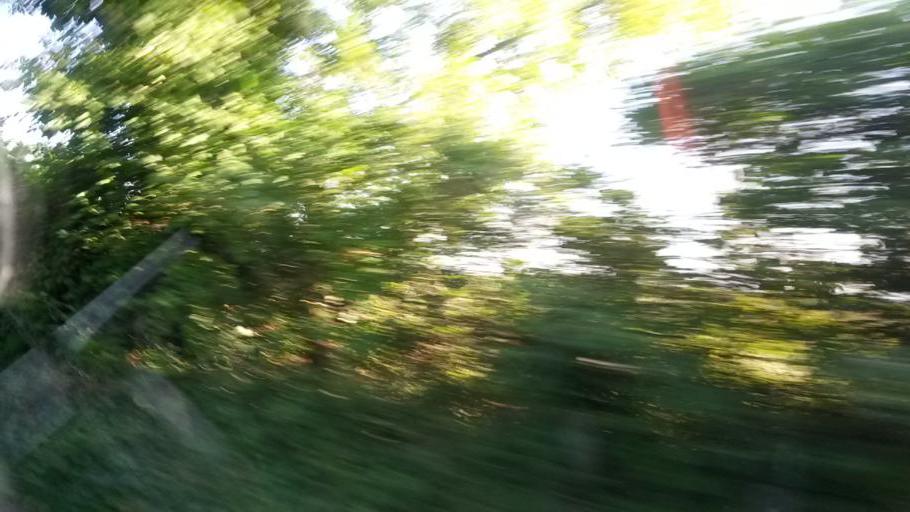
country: IE
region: Leinster
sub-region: An Mhi
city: Ashbourne
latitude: 53.5385
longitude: -6.3680
